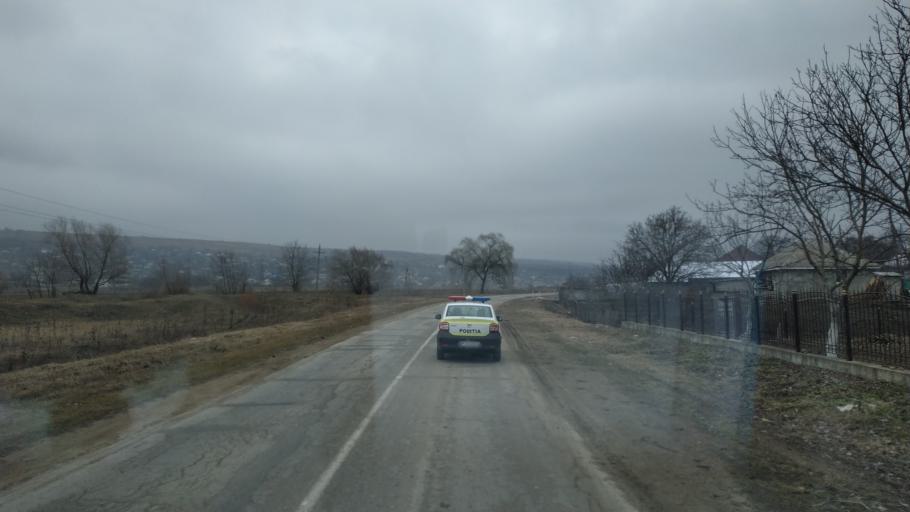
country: MD
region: Hincesti
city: Hincesti
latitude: 46.9768
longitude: 28.4670
